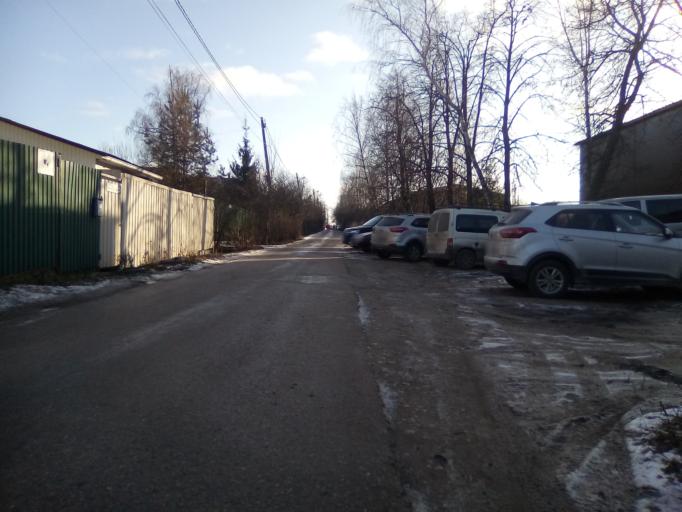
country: RU
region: Moskovskaya
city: Lesnoy Gorodok
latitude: 55.6643
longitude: 37.1816
